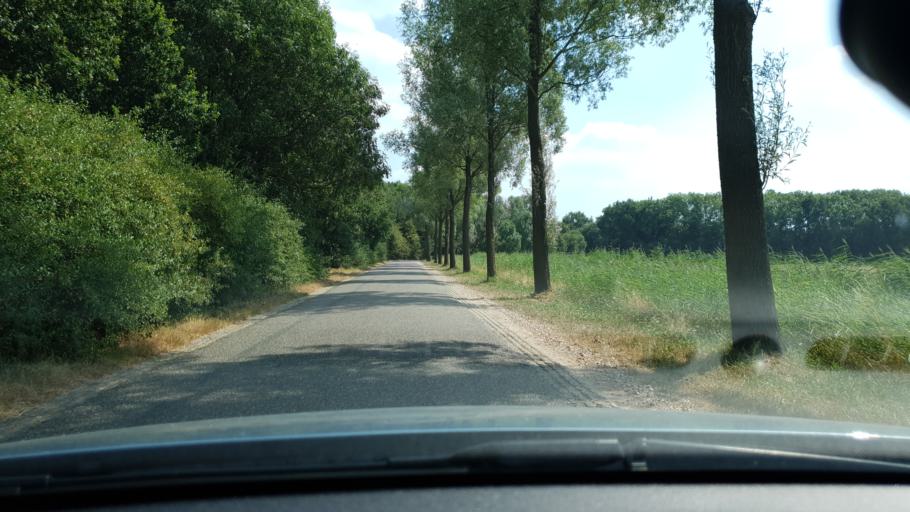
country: NL
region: Gelderland
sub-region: Gemeente Wijchen
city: Bergharen
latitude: 51.8481
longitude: 5.6858
